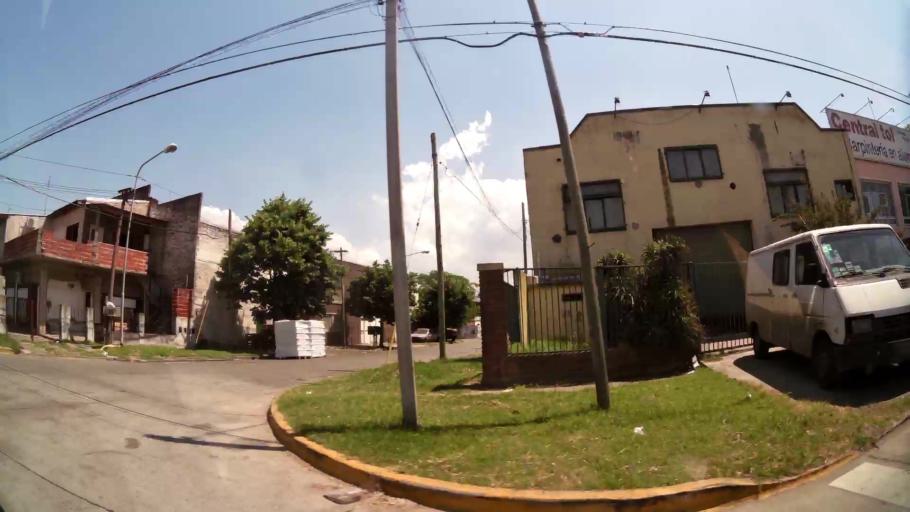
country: AR
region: Buenos Aires
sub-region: Partido de Tigre
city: Tigre
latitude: -34.4431
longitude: -58.5816
